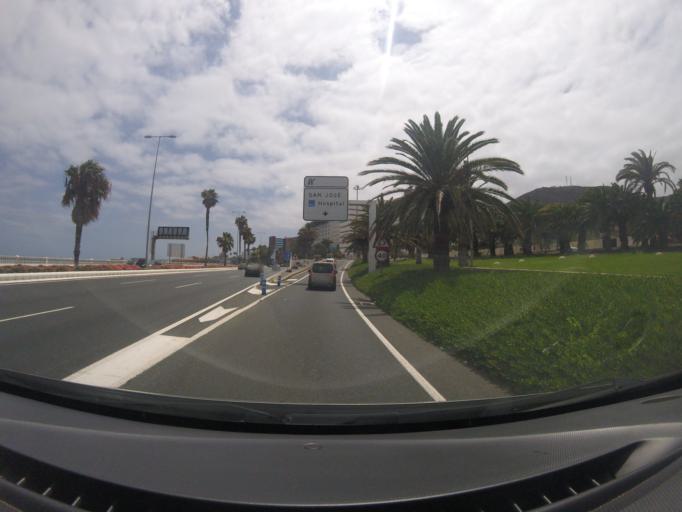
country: ES
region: Canary Islands
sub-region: Provincia de Las Palmas
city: Las Palmas de Gran Canaria
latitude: 28.0854
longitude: -15.4166
